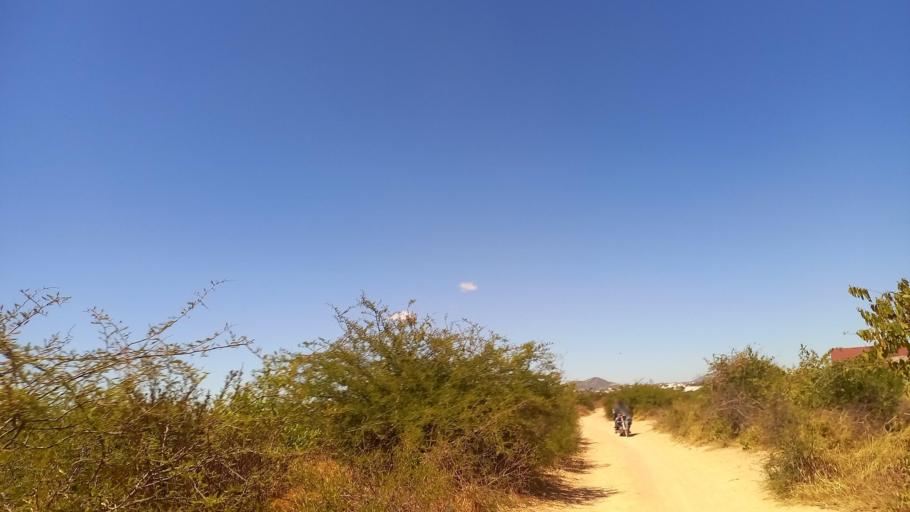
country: TZ
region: Dodoma
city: Dodoma
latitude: -6.1199
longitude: 35.6973
